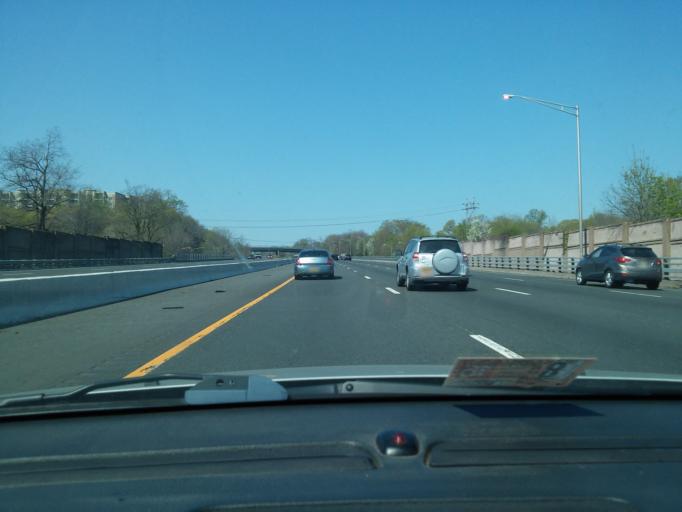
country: US
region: New Jersey
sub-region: Union County
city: Springfield
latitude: 40.7116
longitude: -74.3255
